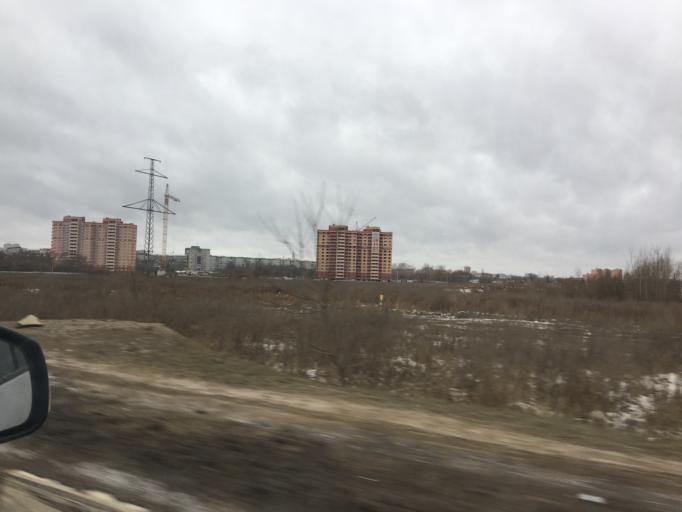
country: RU
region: Tula
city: Tula
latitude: 54.1836
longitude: 37.6506
